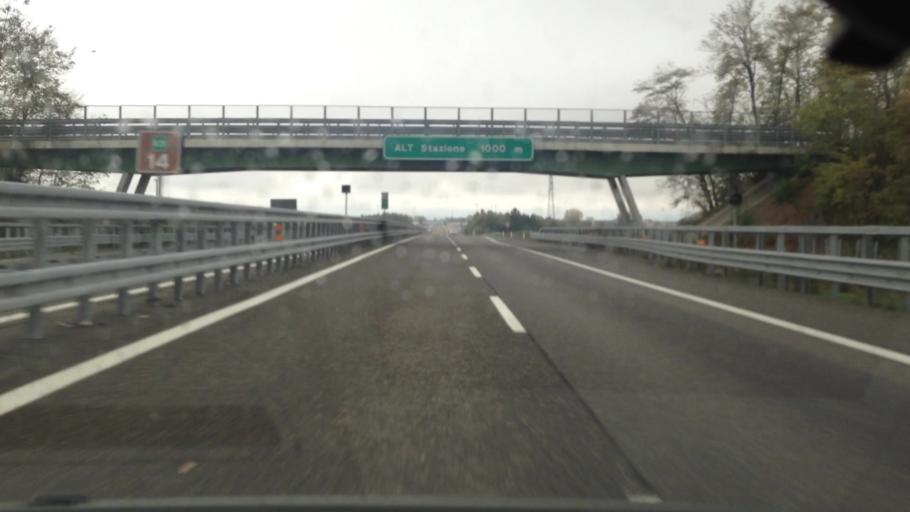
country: IT
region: Piedmont
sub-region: Provincia di Asti
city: Villanova d'Asti
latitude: 44.9514
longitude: 7.9384
